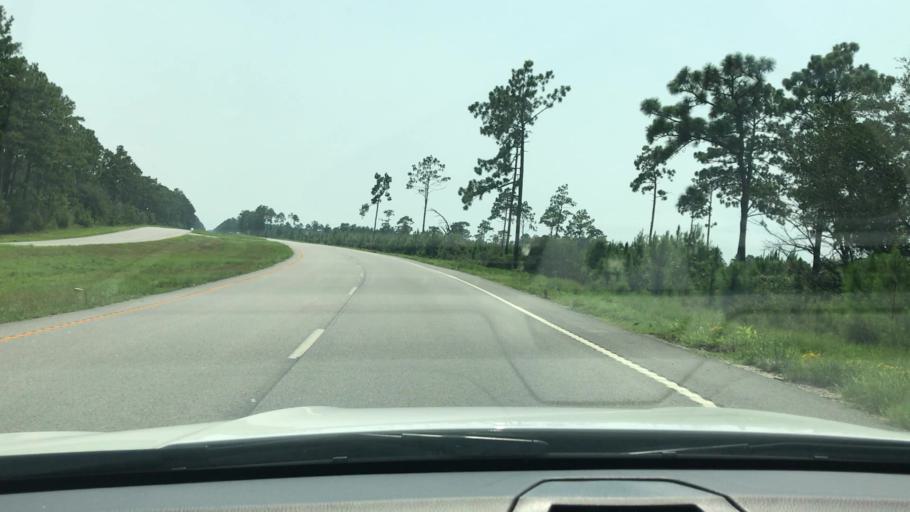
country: US
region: South Carolina
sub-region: Georgetown County
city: Georgetown
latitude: 33.1797
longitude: -79.4133
